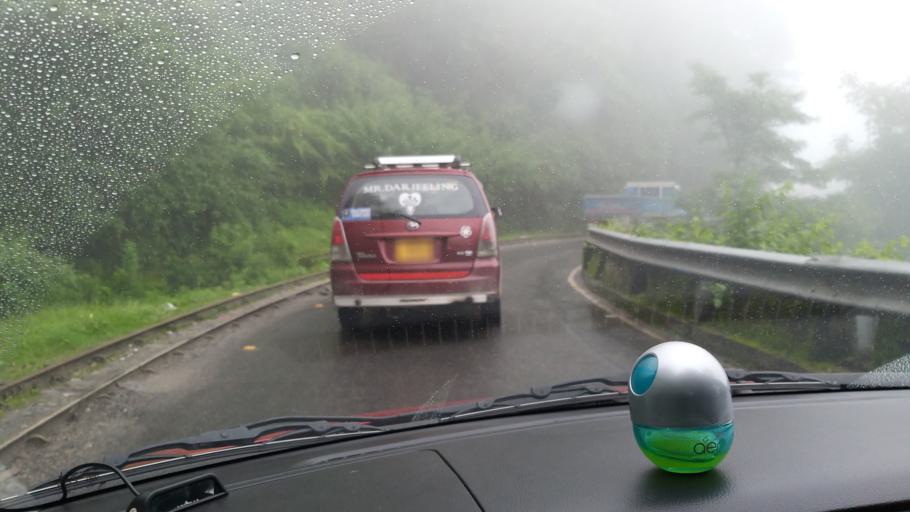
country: IN
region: West Bengal
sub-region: Darjiling
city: Karsiyang
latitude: 26.9560
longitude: 88.2815
